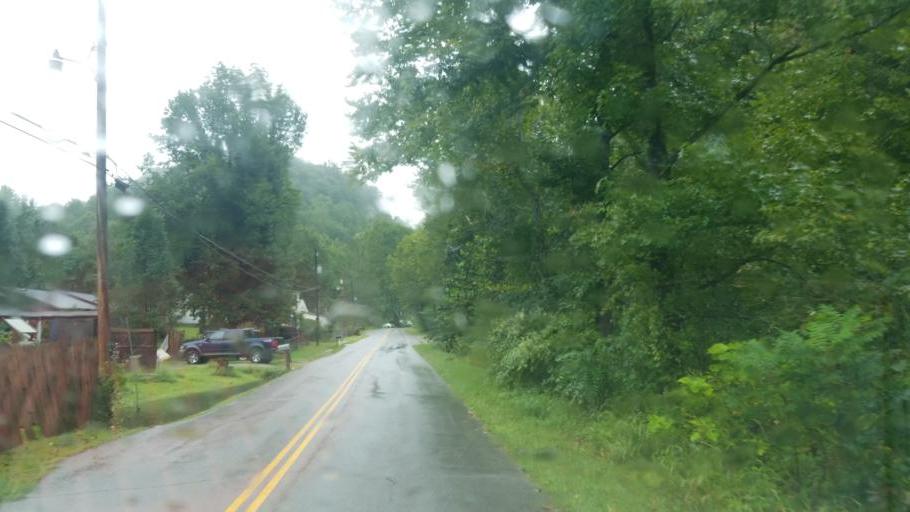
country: US
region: Ohio
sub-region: Scioto County
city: West Portsmouth
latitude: 38.7524
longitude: -83.1004
